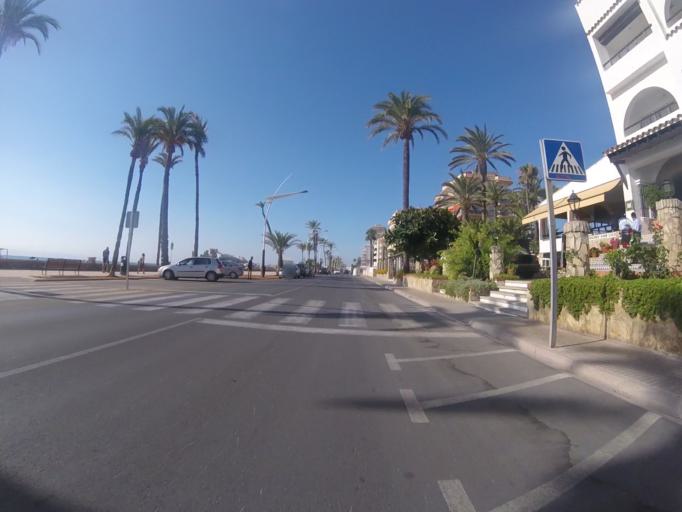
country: ES
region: Valencia
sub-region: Provincia de Castello
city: Peniscola
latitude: 40.3691
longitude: 0.4041
